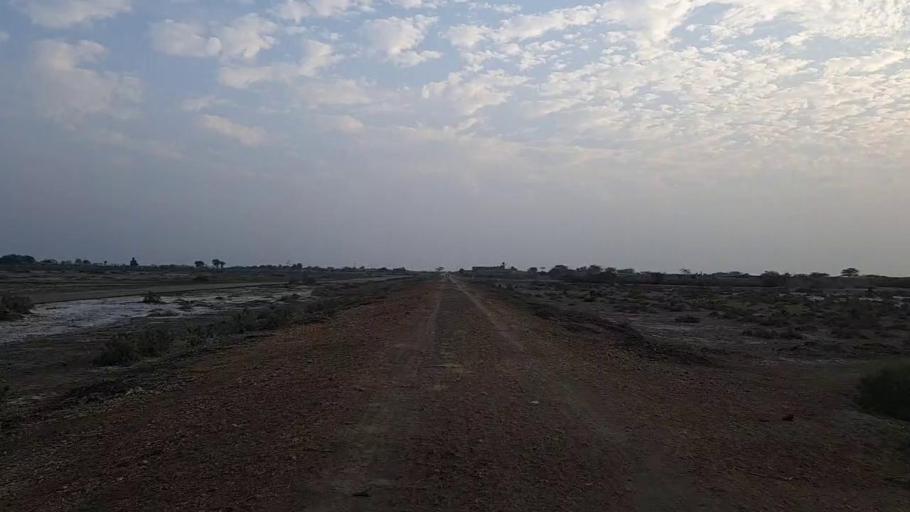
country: PK
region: Sindh
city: Pithoro
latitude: 25.4621
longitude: 69.3460
